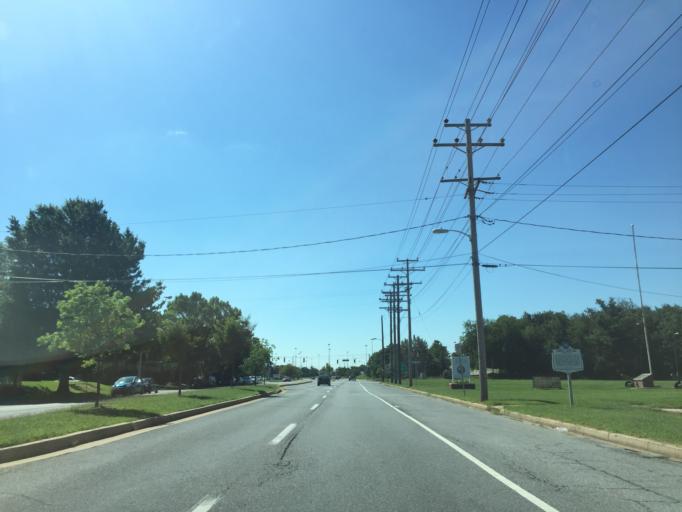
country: US
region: Maryland
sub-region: Baltimore County
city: Dundalk
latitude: 39.2527
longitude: -76.5216
